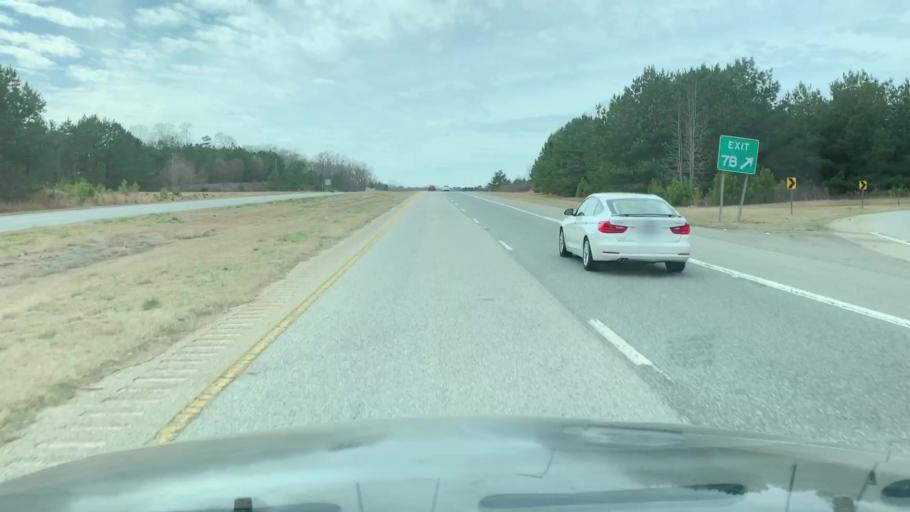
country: US
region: South Carolina
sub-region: Greenville County
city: Golden Grove
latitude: 34.7236
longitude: -82.3893
